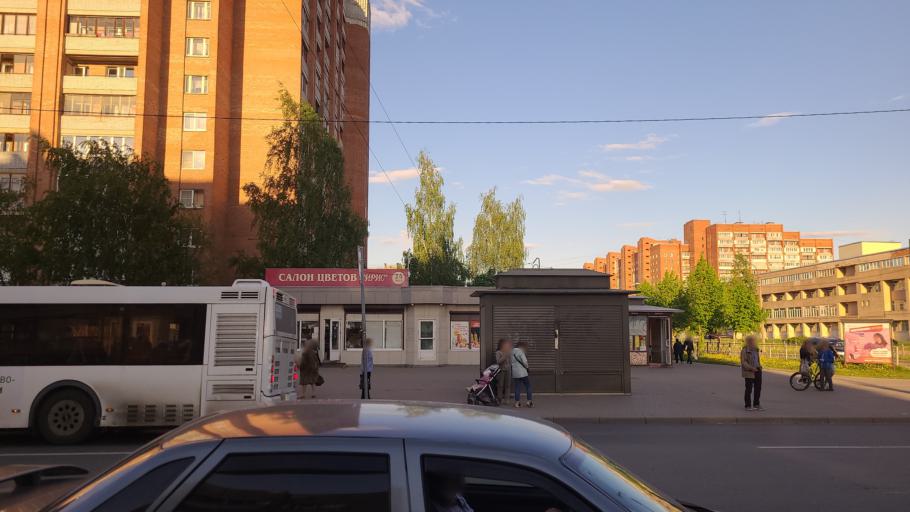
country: RU
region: St.-Petersburg
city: Kolpino
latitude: 59.7357
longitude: 30.5792
